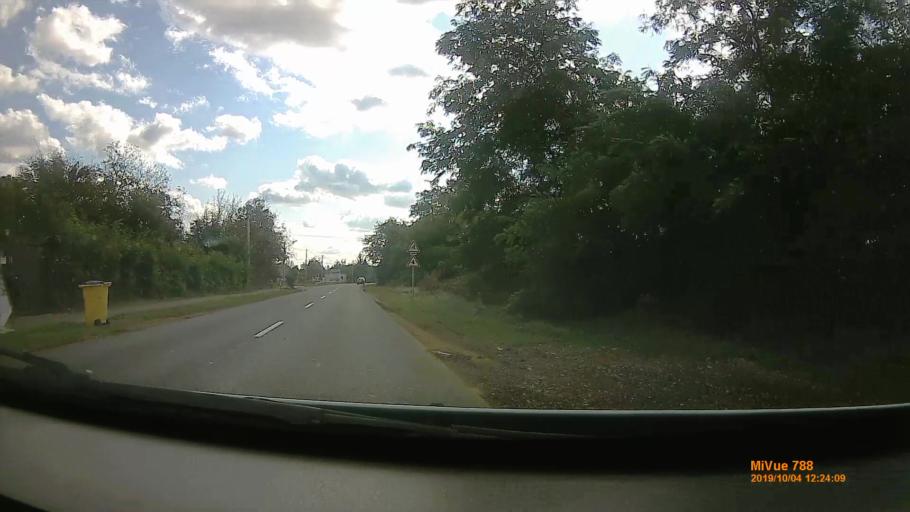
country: HU
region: Szabolcs-Szatmar-Bereg
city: Nyiregyhaza
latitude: 47.9990
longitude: 21.7014
